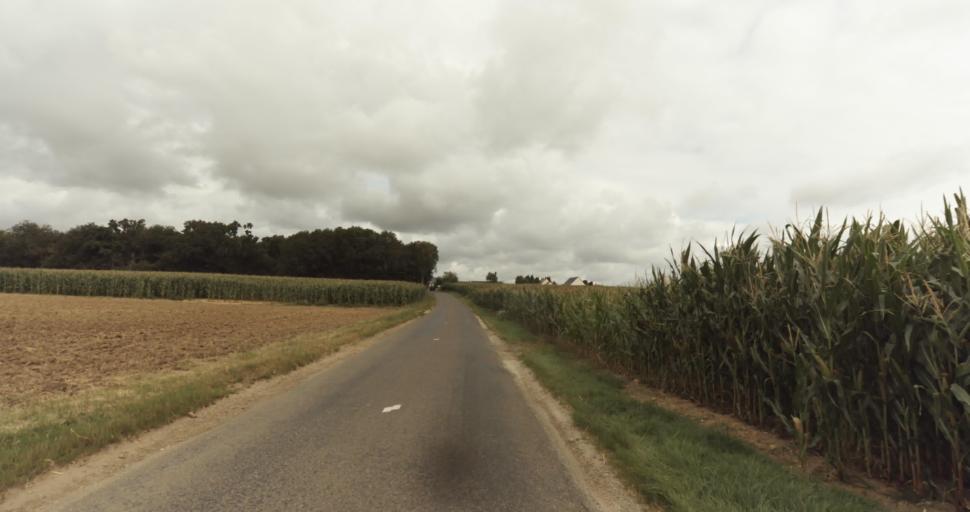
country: FR
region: Haute-Normandie
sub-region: Departement de l'Eure
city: Menilles
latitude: 48.9555
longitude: 1.2991
